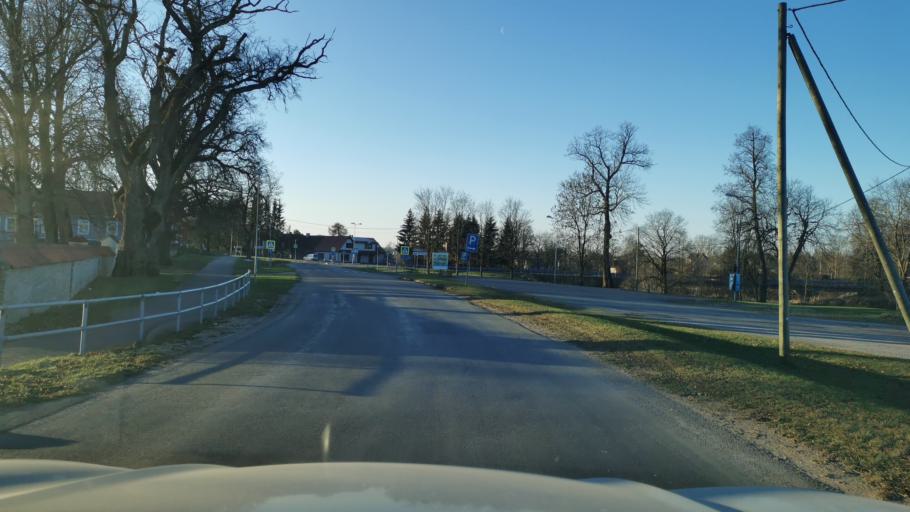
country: EE
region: Ida-Virumaa
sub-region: Puessi linn
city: Pussi
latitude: 59.3373
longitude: 27.0132
